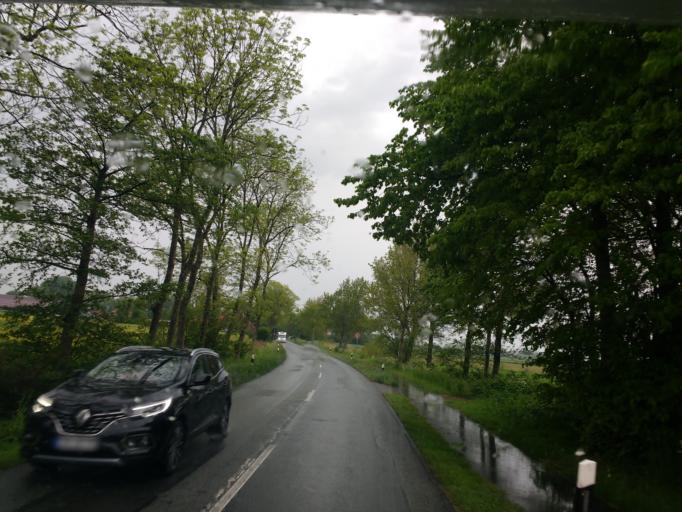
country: DE
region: Lower Saxony
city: Schillig
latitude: 53.7000
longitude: 7.9970
